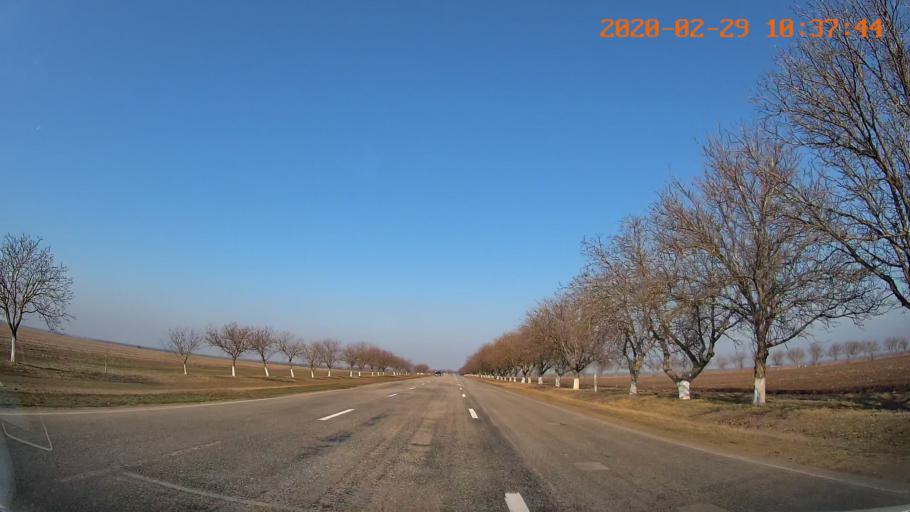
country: MD
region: Anenii Noi
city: Varnita
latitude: 47.0092
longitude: 29.4848
